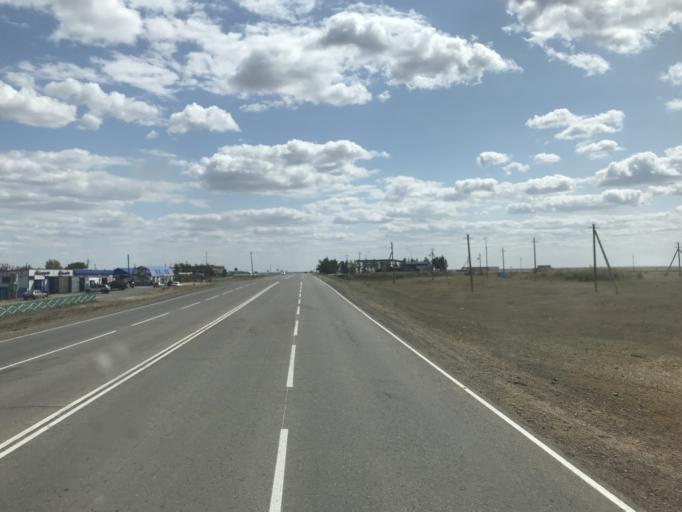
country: KZ
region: Qostanay
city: Qusmuryn
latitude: 52.3606
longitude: 64.1054
